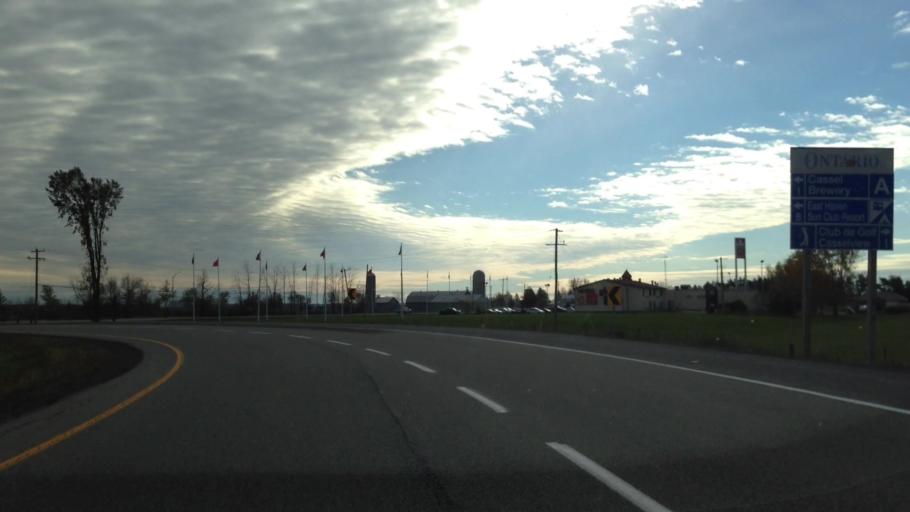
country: CA
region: Ontario
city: Casselman
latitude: 45.3014
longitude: -75.0814
